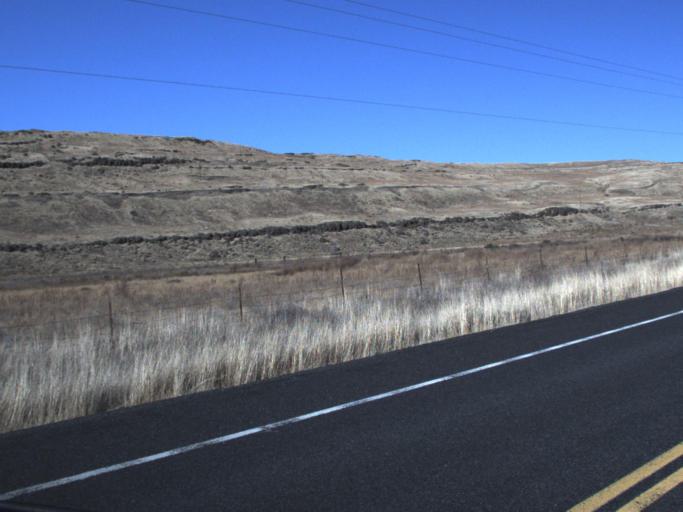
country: US
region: Washington
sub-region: Adams County
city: Ritzville
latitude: 46.6961
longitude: -118.4241
